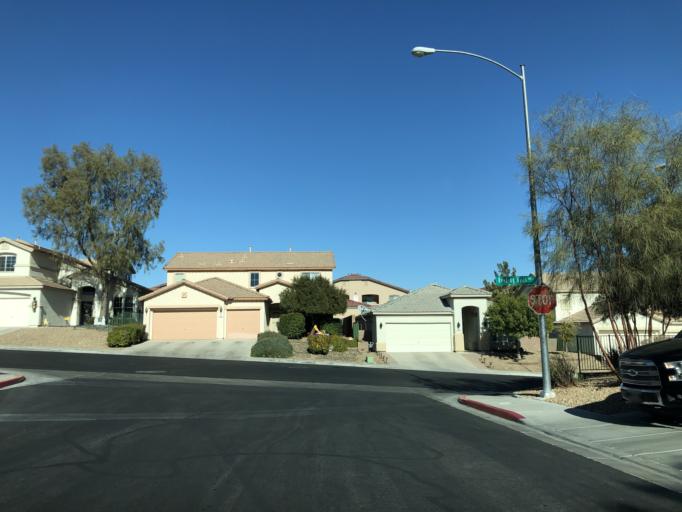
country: US
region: Nevada
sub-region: Clark County
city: Whitney
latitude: 36.0017
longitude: -115.0885
